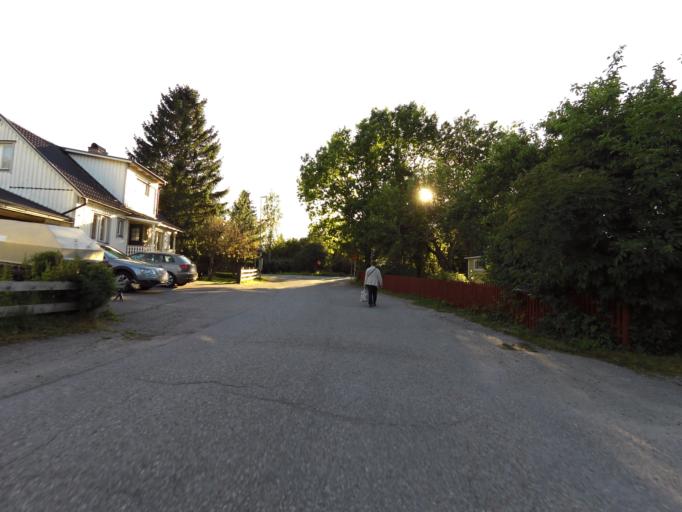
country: SE
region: Gaevleborg
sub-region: Gavle Kommun
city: Gavle
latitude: 60.7110
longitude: 17.1476
